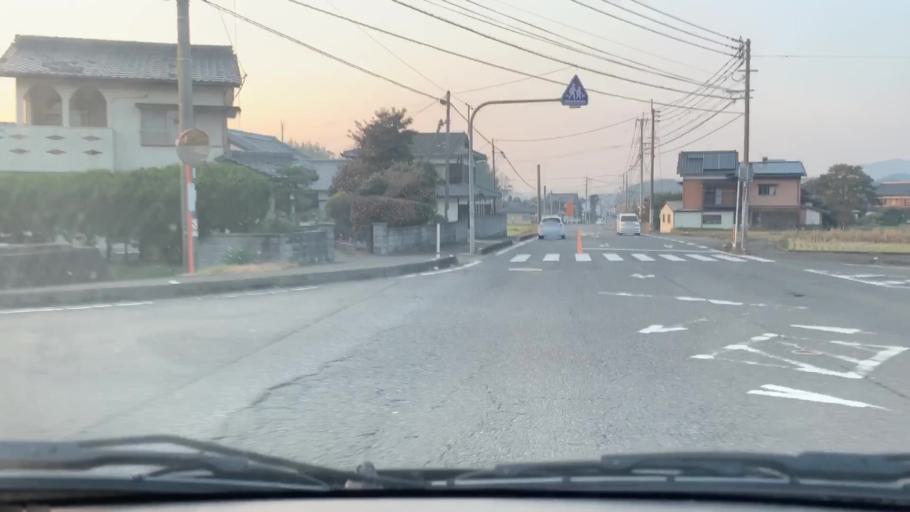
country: JP
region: Saga Prefecture
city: Imaricho-ko
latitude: 33.2657
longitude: 129.9028
